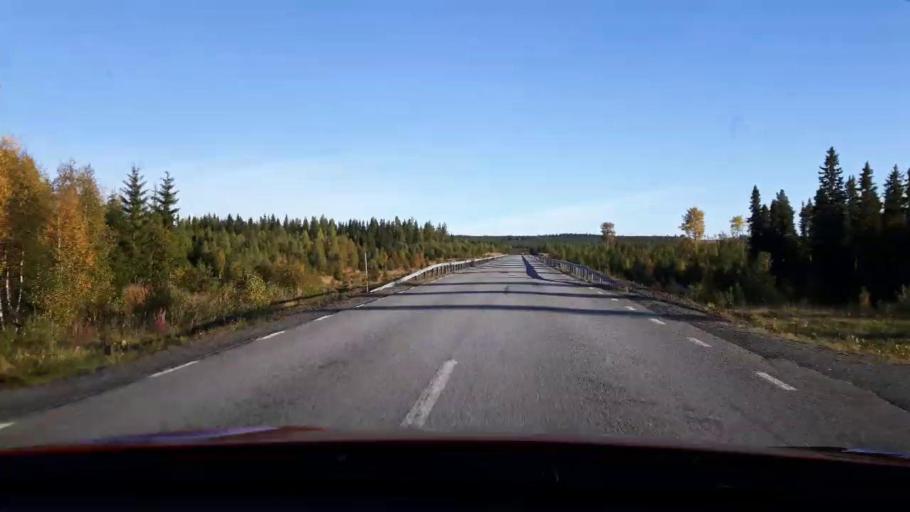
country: SE
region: Jaemtland
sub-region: OEstersunds Kommun
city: Lit
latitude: 63.7749
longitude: 14.7127
